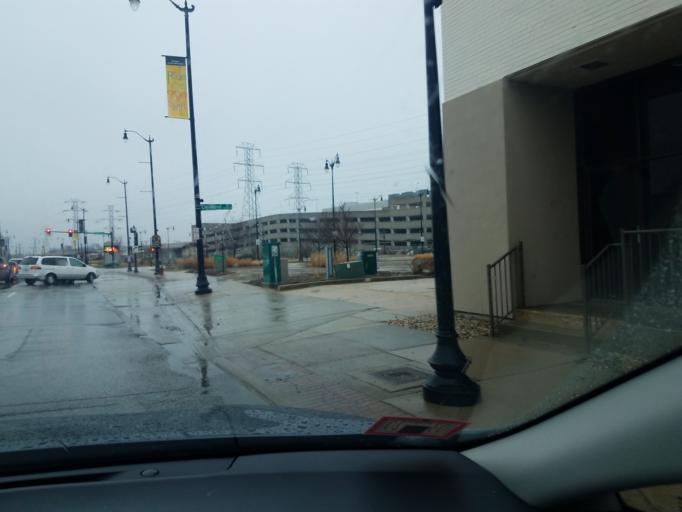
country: US
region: Illinois
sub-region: Cook County
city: Skokie
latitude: 42.0302
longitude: -87.7476
